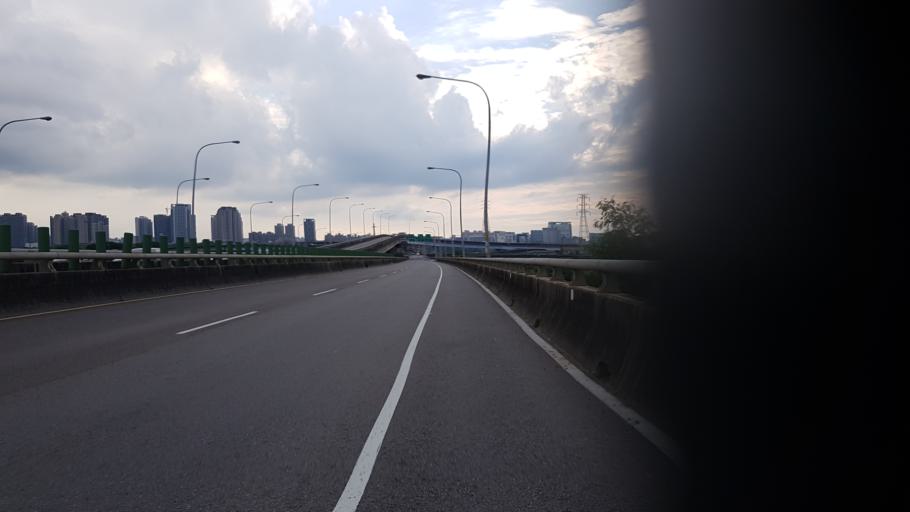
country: TW
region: Taiwan
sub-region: Hsinchu
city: Zhubei
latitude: 24.8088
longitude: 121.0198
